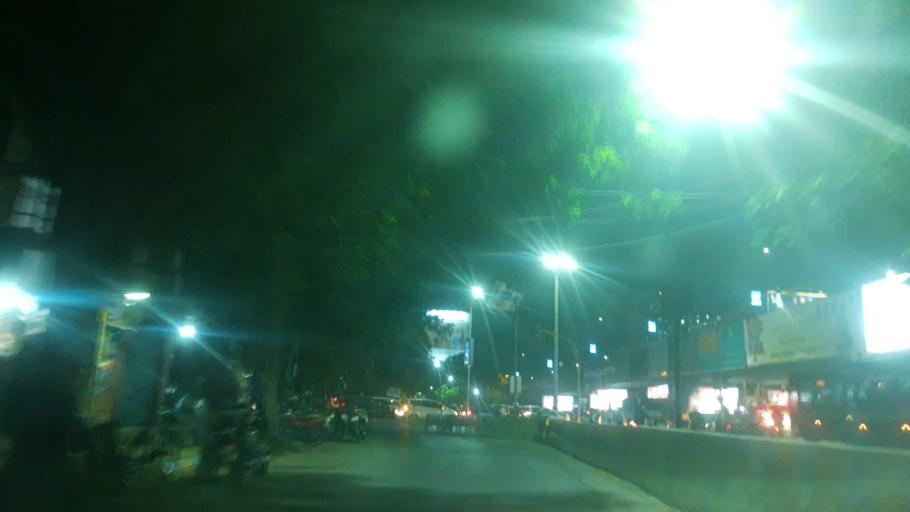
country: IN
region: Maharashtra
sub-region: Thane
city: Thane
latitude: 19.1891
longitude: 72.9638
